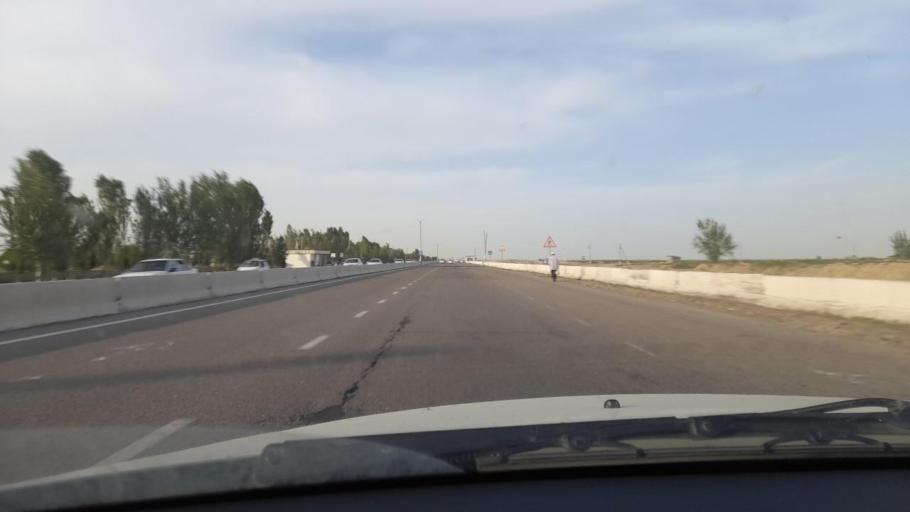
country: UZ
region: Jizzax
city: Dustlik
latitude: 40.4418
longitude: 68.2388
